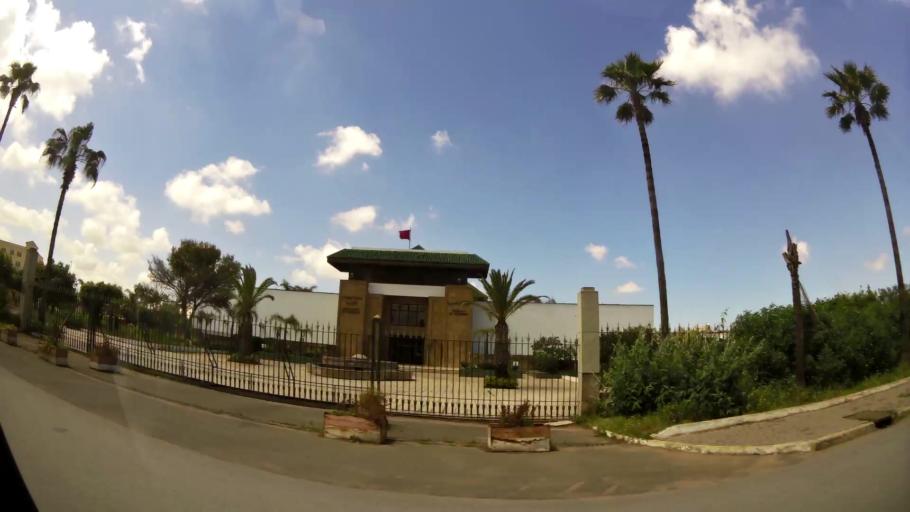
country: MA
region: Grand Casablanca
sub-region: Casablanca
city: Casablanca
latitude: 33.5591
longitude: -7.5637
